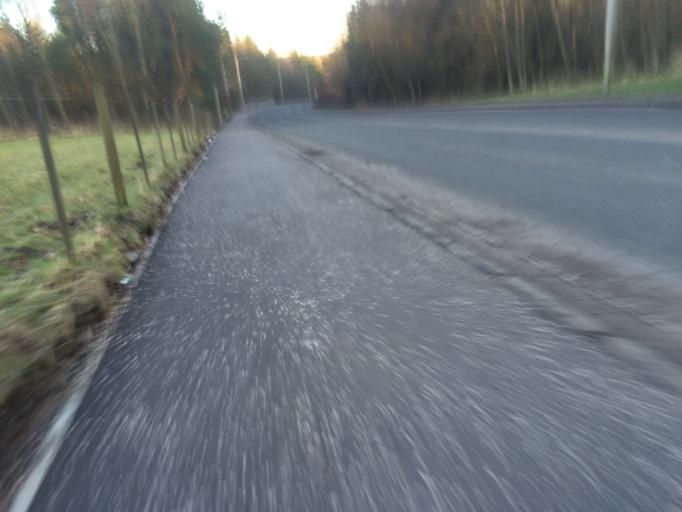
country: GB
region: Scotland
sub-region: Fife
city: Lochgelly
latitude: 56.1442
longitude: -3.3222
